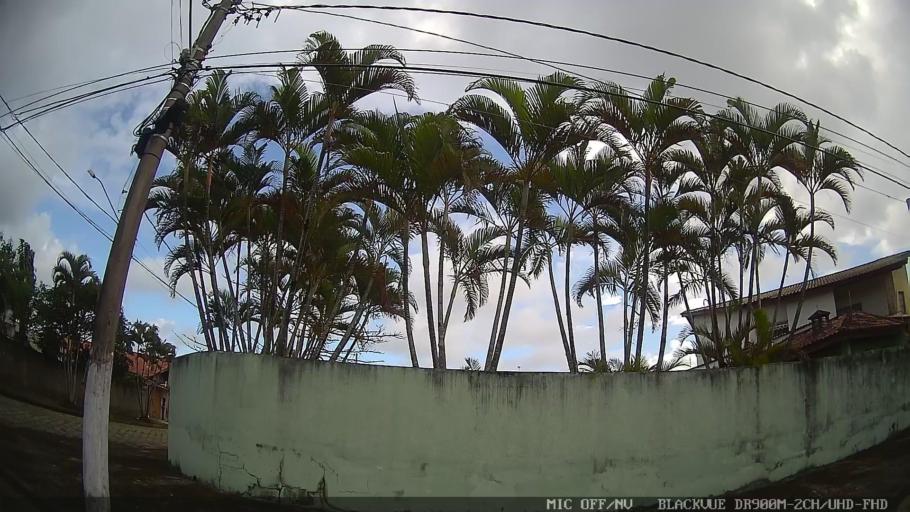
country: BR
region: Sao Paulo
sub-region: Itanhaem
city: Itanhaem
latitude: -24.2181
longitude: -46.8495
